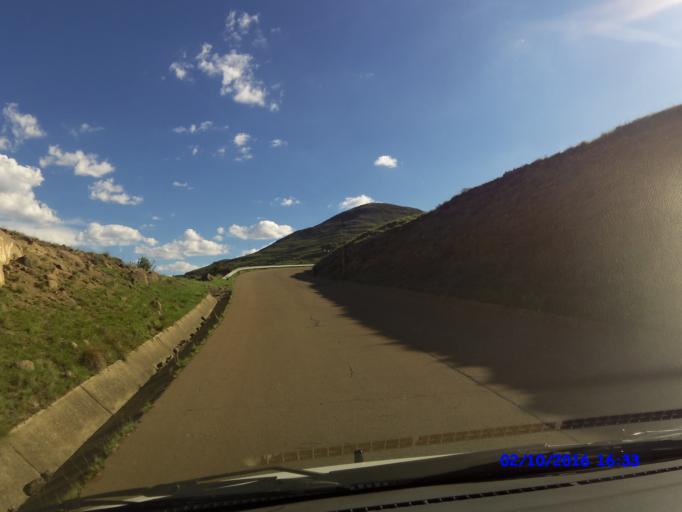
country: LS
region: Maseru
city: Nako
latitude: -29.4892
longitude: 28.0640
